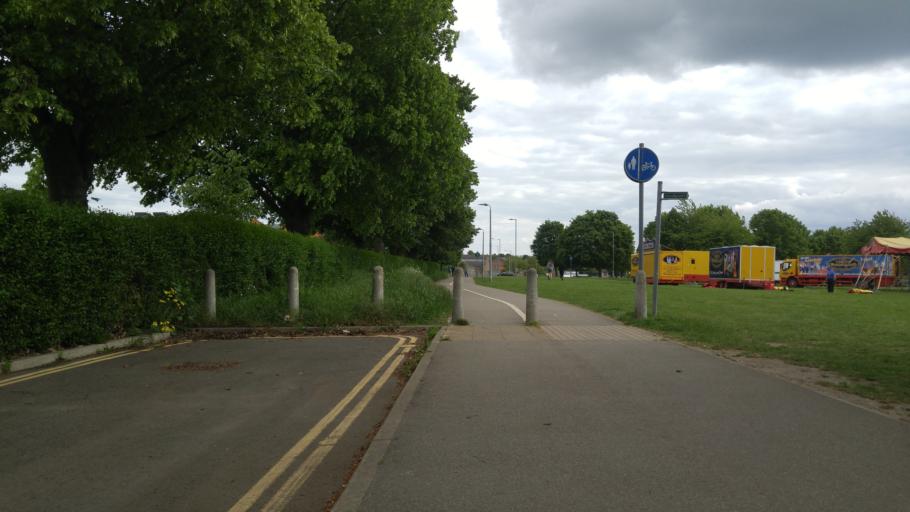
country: GB
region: England
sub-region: Essex
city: Colchester
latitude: 51.8820
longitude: 0.8999
